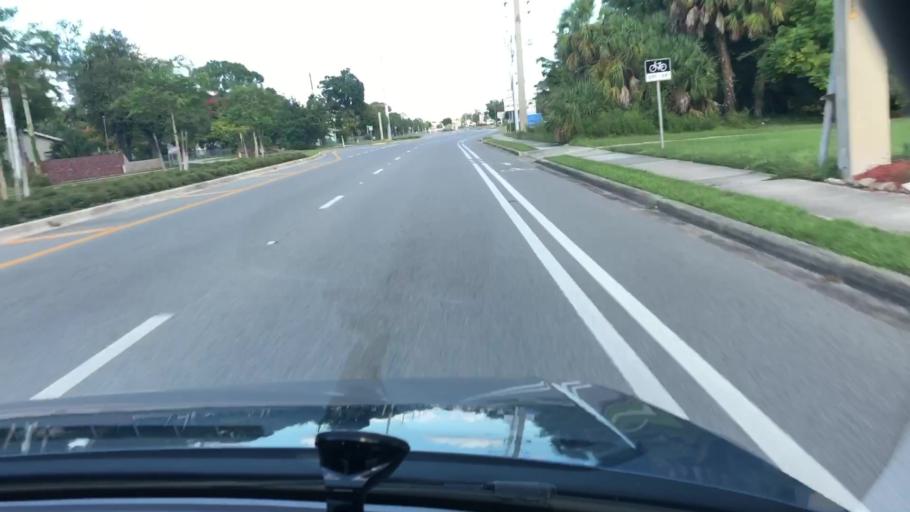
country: US
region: Florida
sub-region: Volusia County
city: South Daytona
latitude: 29.1789
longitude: -81.0197
